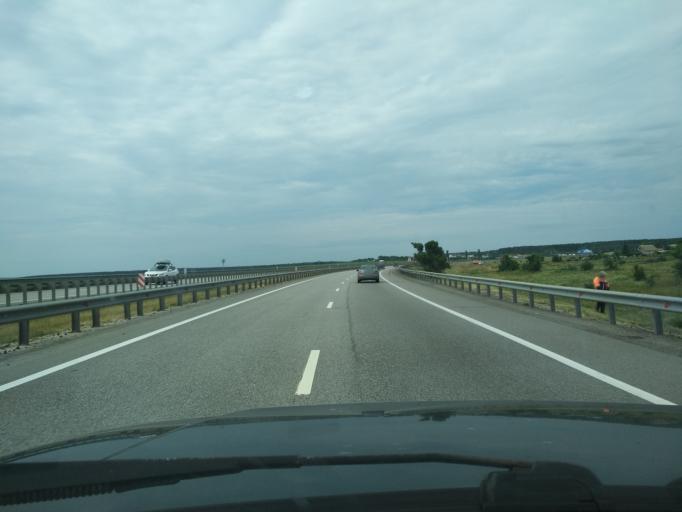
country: RU
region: Lipetsk
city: Khlevnoye
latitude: 52.0657
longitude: 39.1800
